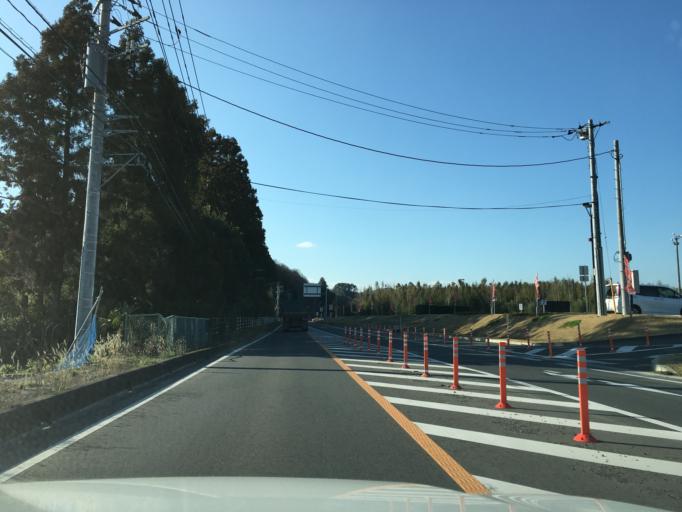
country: JP
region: Ibaraki
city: Omiya
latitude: 36.5967
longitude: 140.4088
